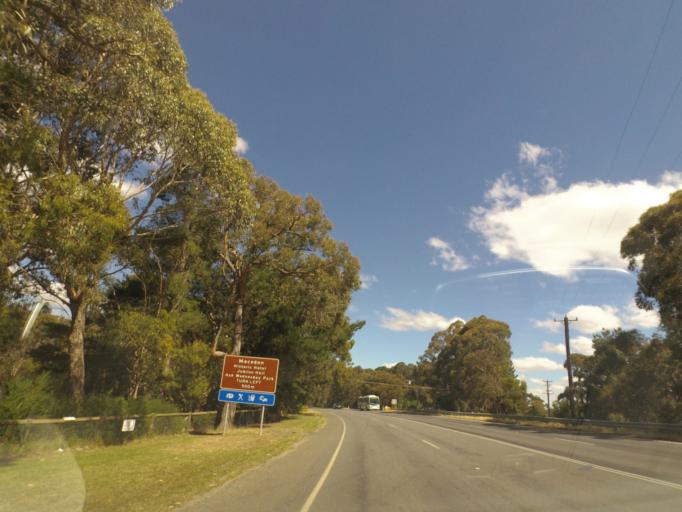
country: AU
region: Victoria
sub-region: Hume
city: Sunbury
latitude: -37.4286
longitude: 144.5545
